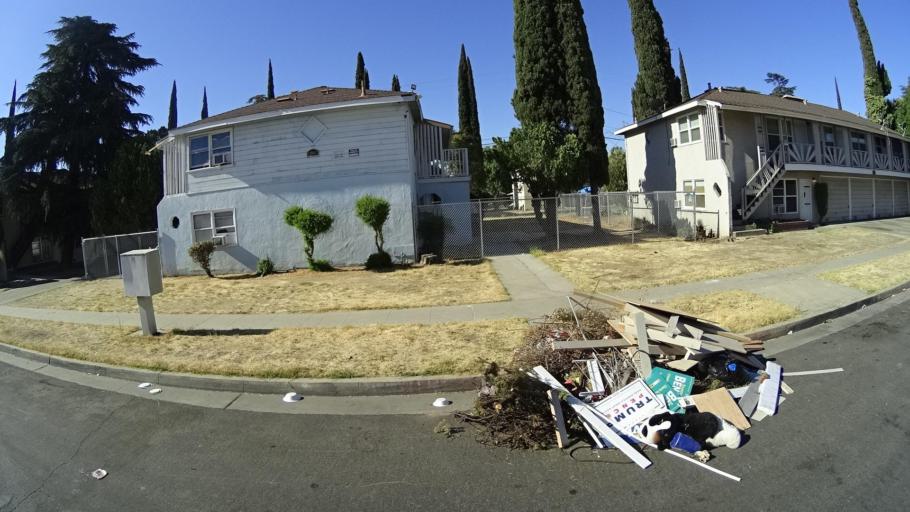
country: US
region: California
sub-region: Fresno County
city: Fresno
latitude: 36.7793
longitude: -119.7869
